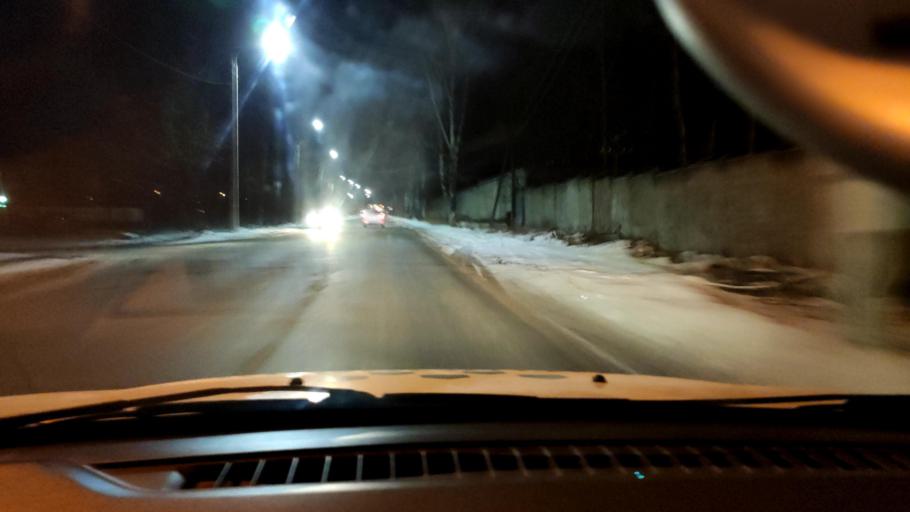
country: RU
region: Perm
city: Kultayevo
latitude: 57.9893
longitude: 55.9255
